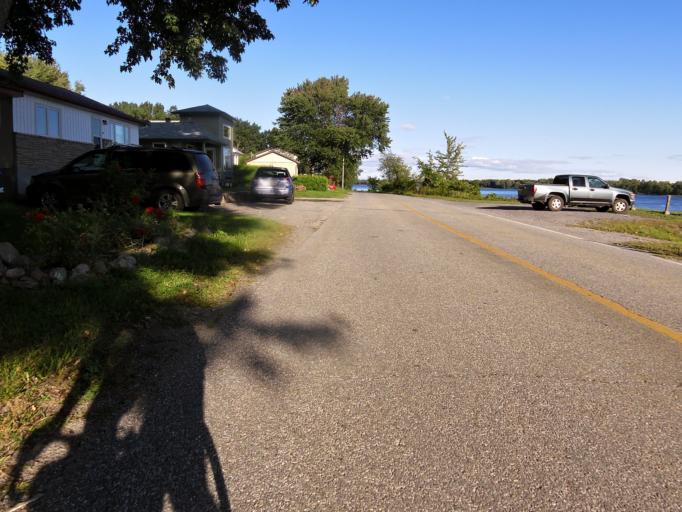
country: CA
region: Quebec
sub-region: Outaouais
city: Gatineau
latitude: 45.4752
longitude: -75.6070
